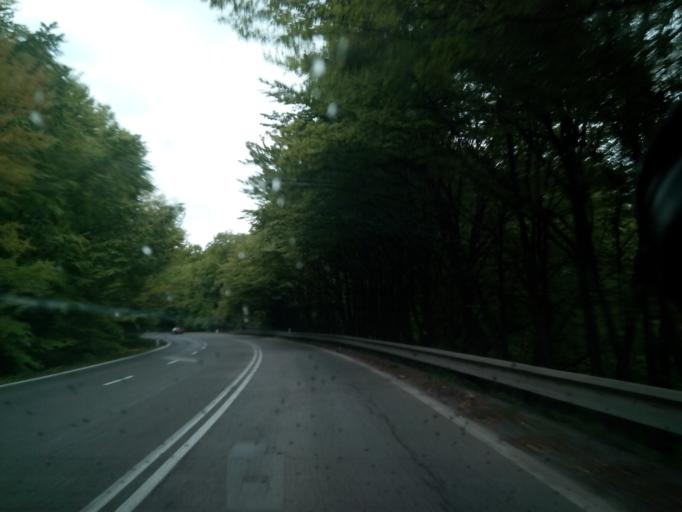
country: SK
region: Kosicky
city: Kosice
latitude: 48.7355
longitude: 21.3783
